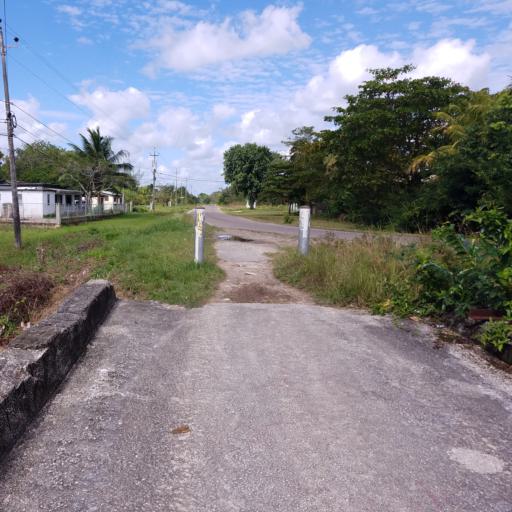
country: BZ
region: Belize
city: Belize City
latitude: 17.5608
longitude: -88.4048
